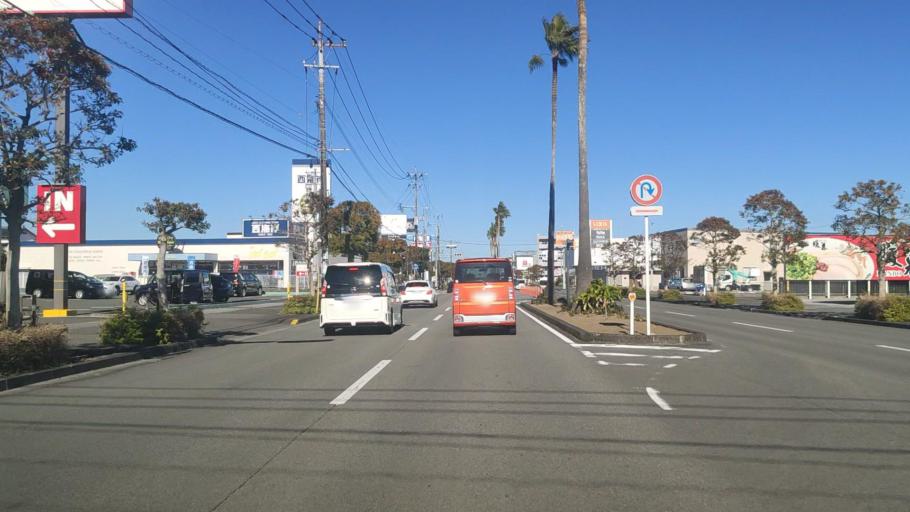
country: JP
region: Miyazaki
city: Miyazaki-shi
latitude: 31.9127
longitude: 131.4480
